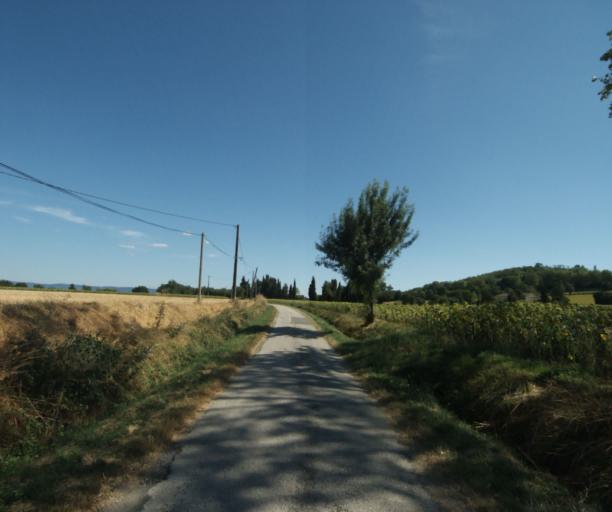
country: FR
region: Midi-Pyrenees
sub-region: Departement de la Haute-Garonne
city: Saint-Felix-Lauragais
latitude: 43.4987
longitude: 1.8993
